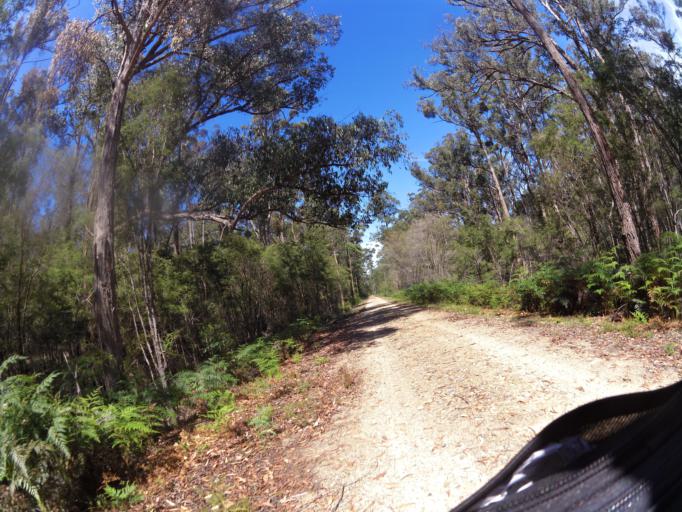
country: AU
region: Victoria
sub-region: East Gippsland
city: Lakes Entrance
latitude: -37.7213
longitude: 148.1171
